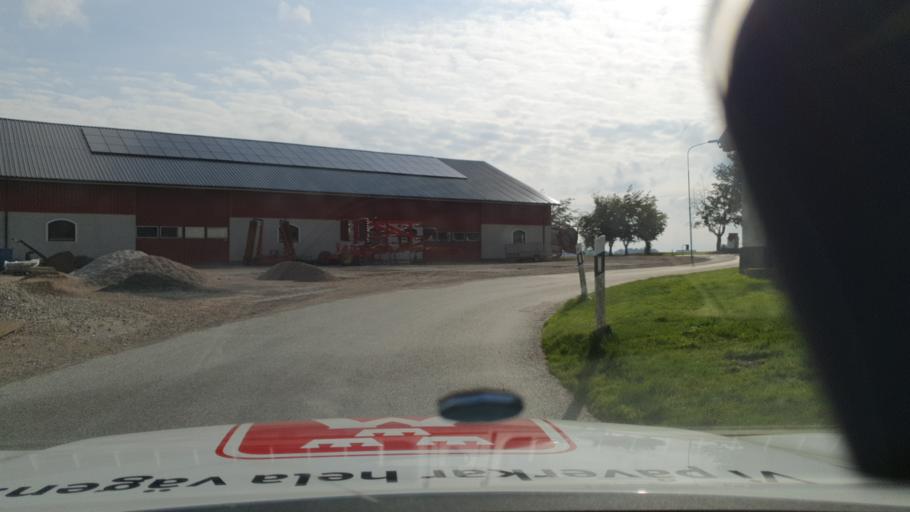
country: SE
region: Skane
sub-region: Trelleborgs Kommun
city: Trelleborg
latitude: 55.4241
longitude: 13.1099
